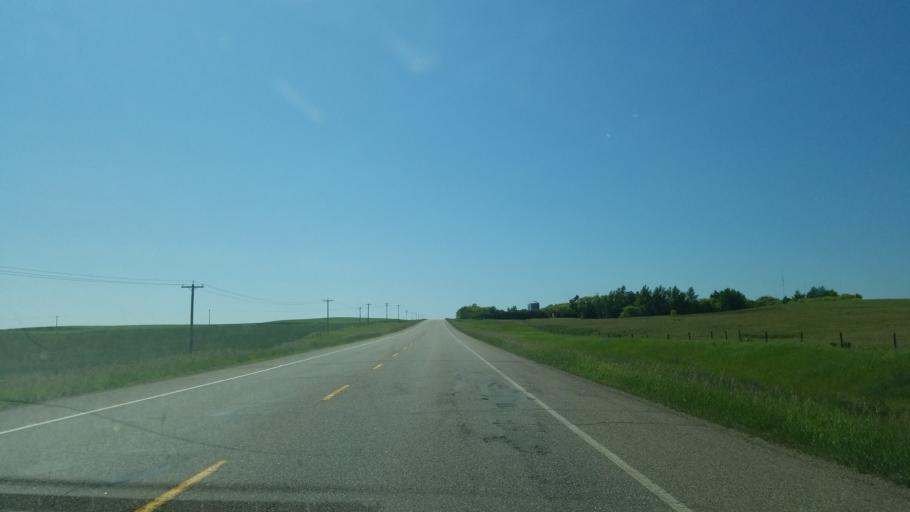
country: CA
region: Alberta
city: Provost
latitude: 52.3613
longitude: -110.1439
